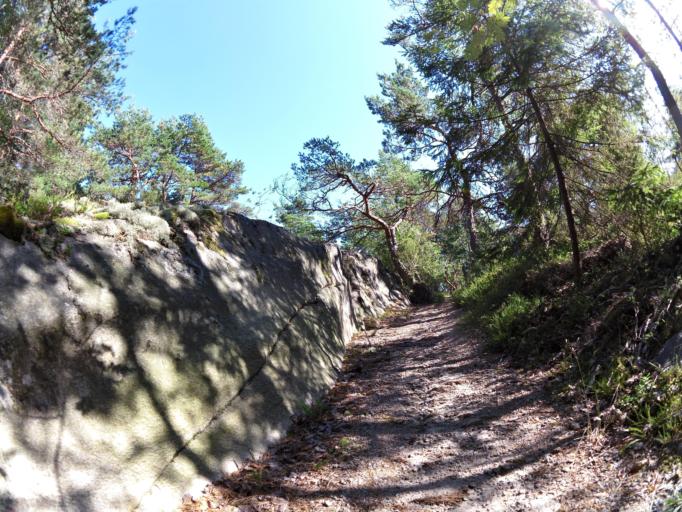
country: NO
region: Ostfold
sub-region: Fredrikstad
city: Fredrikstad
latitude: 59.1687
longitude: 10.8453
